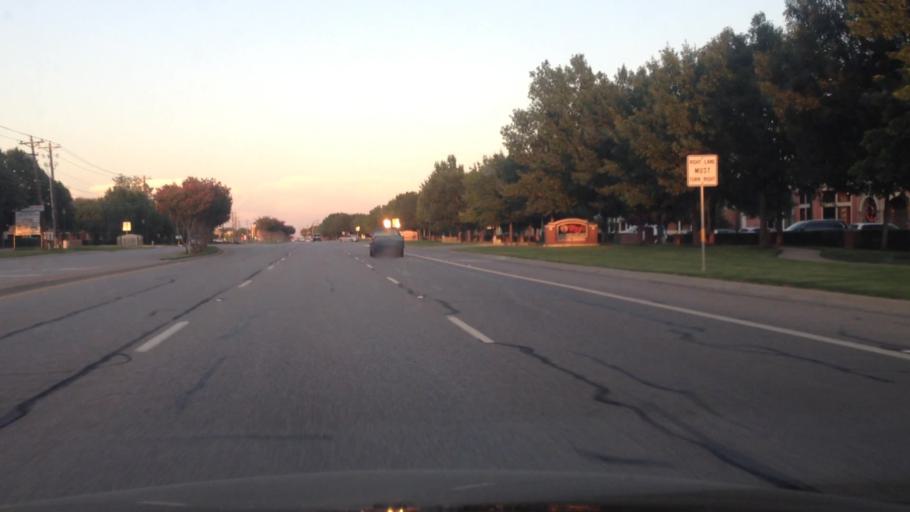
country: US
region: Texas
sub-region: Tarrant County
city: Keller
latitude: 32.9342
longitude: -97.2269
